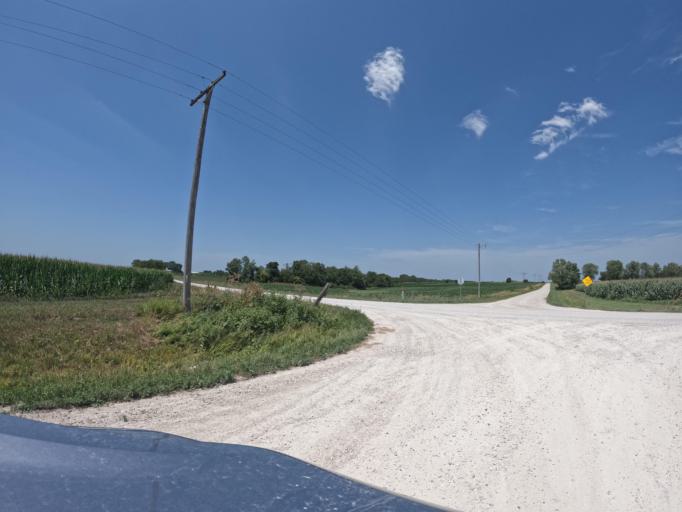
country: US
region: Iowa
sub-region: Henry County
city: Mount Pleasant
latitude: 40.9409
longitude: -91.6460
